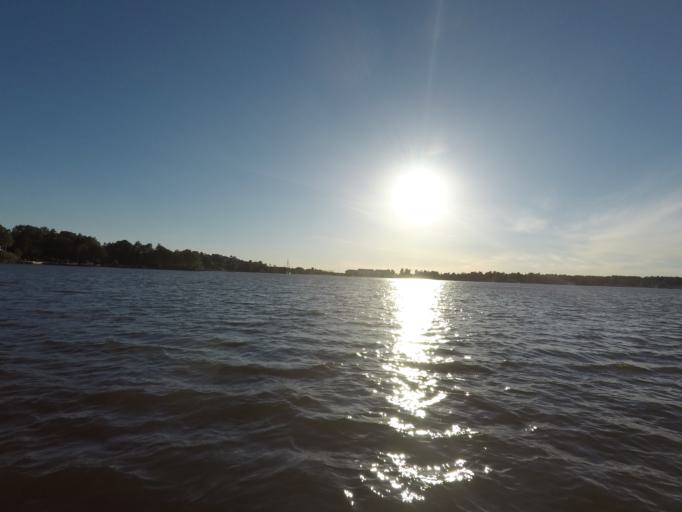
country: SE
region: Soedermanland
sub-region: Eskilstuna Kommun
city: Kvicksund
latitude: 59.4542
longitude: 16.3347
